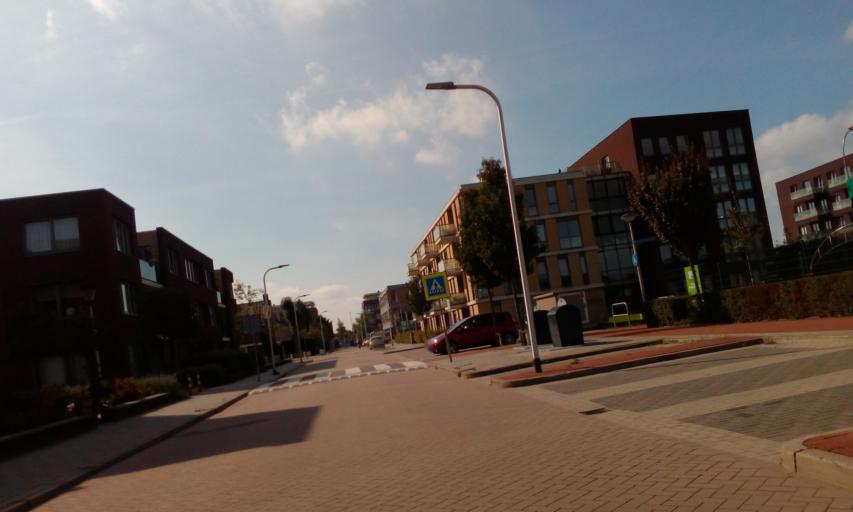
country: NL
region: South Holland
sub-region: Gemeente Katwijk
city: Rijnsburg
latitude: 52.1912
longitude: 4.4355
